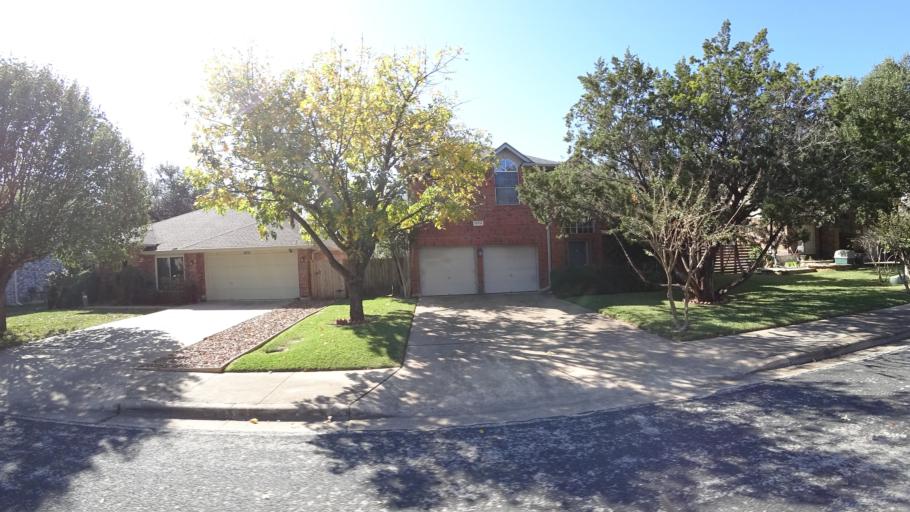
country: US
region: Texas
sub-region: Williamson County
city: Jollyville
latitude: 30.4158
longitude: -97.7647
